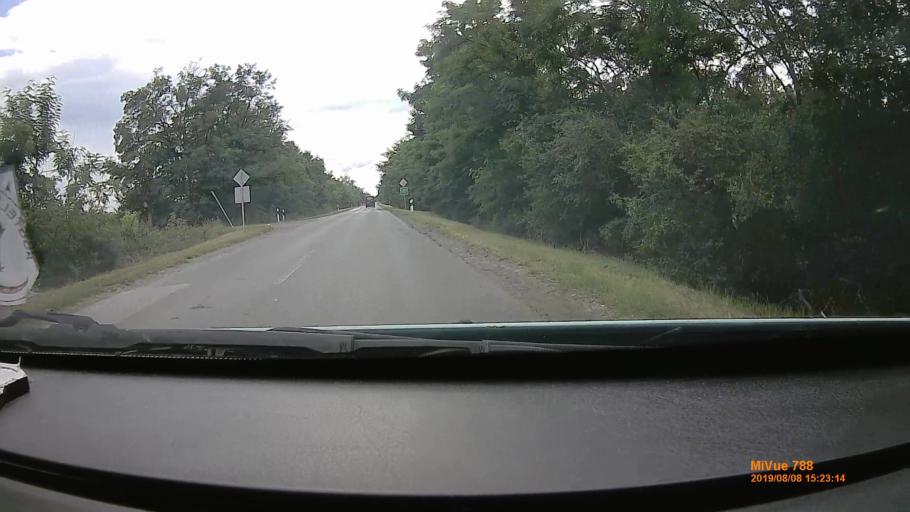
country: HU
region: Szabolcs-Szatmar-Bereg
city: Tunyogmatolcs
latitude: 47.9576
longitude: 22.4401
